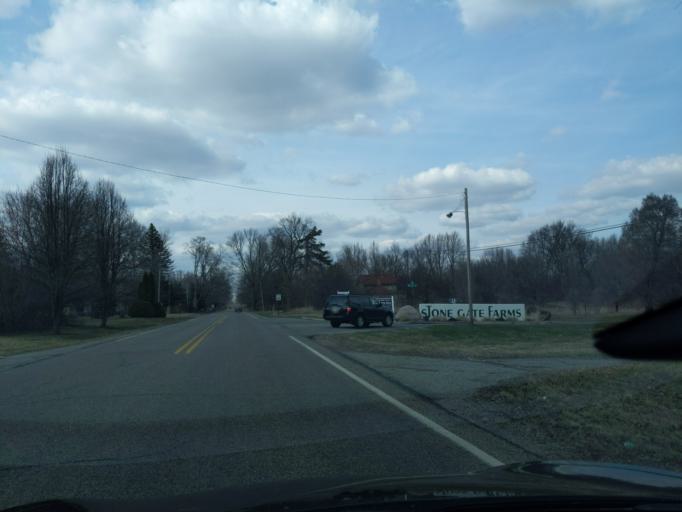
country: US
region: Michigan
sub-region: Jackson County
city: Jackson
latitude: 42.3100
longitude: -84.4136
